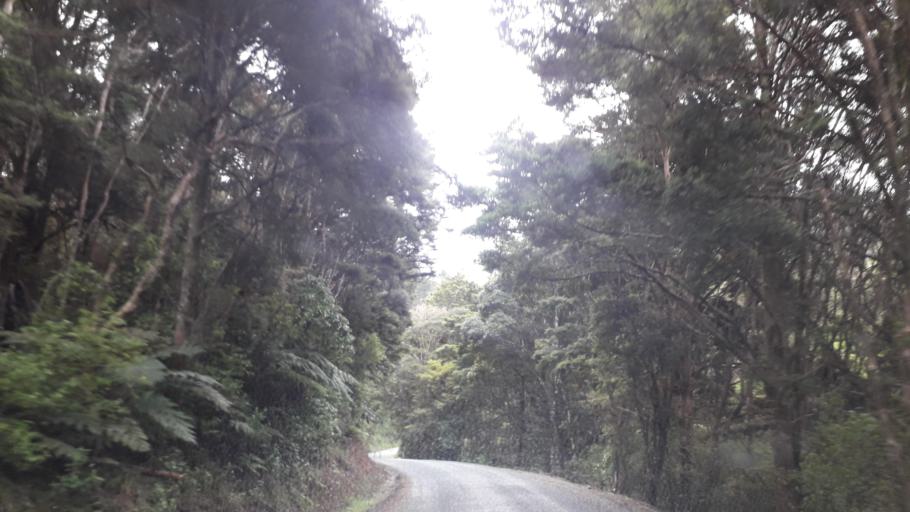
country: NZ
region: Northland
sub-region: Far North District
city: Taipa
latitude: -35.0653
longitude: 173.5493
